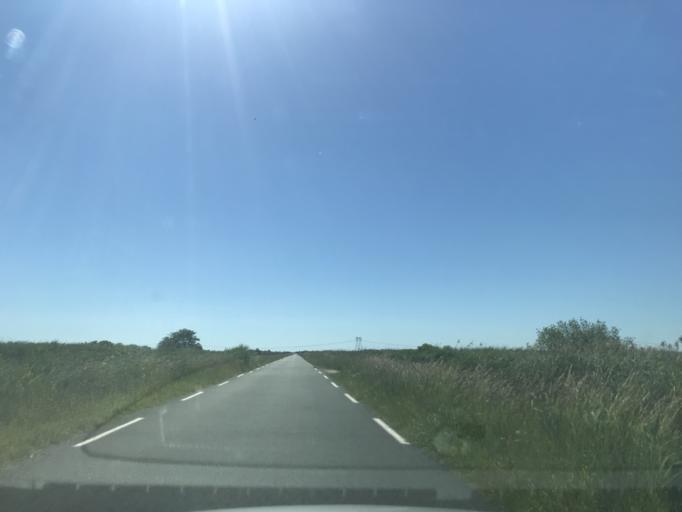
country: FR
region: Aquitaine
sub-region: Departement de la Gironde
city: Saint-Ciers-sur-Gironde
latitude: 45.2901
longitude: -0.6429
